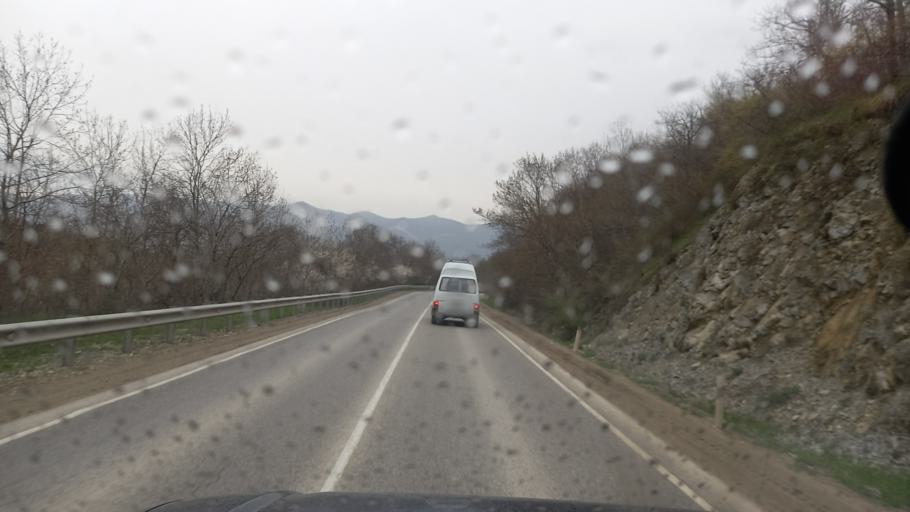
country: RU
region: Krasnodarskiy
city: Gayduk
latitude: 44.7421
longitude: 37.6861
